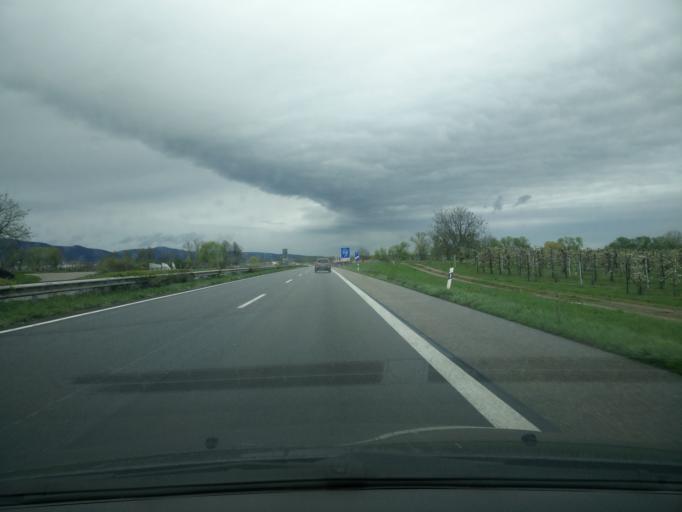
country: DE
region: Rheinland-Pfalz
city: Edesheim
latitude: 49.2646
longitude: 8.1522
